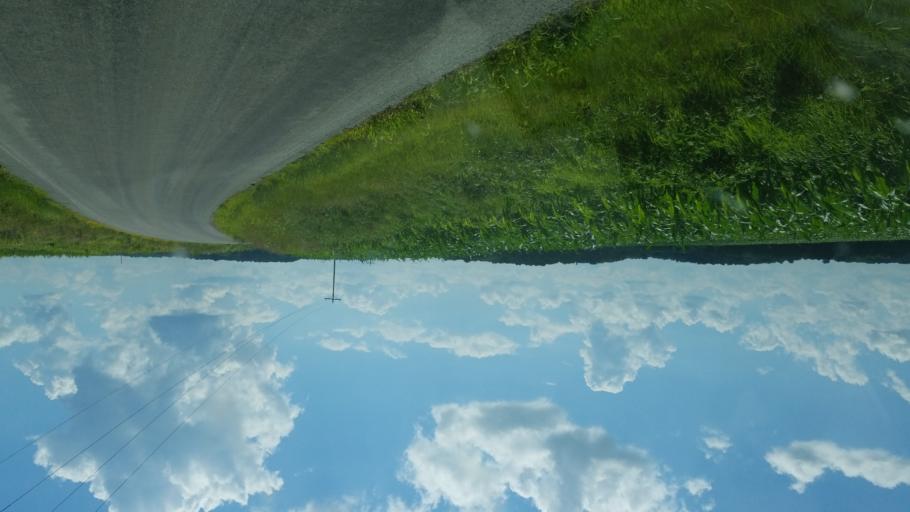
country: US
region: Ohio
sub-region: Highland County
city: Greenfield
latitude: 39.2478
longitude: -83.4236
